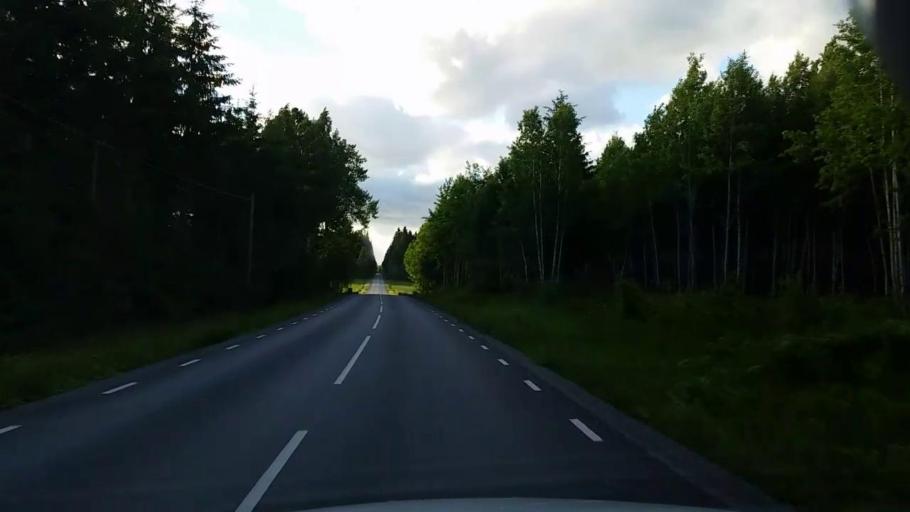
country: SE
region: Vaestmanland
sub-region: Kopings Kommun
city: Kolsva
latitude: 59.6789
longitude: 15.8417
